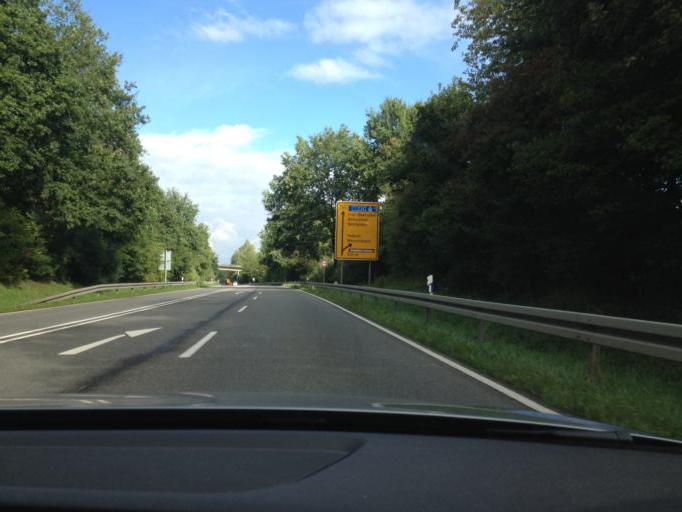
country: DE
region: Saarland
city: Namborn
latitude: 49.4974
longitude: 7.1512
